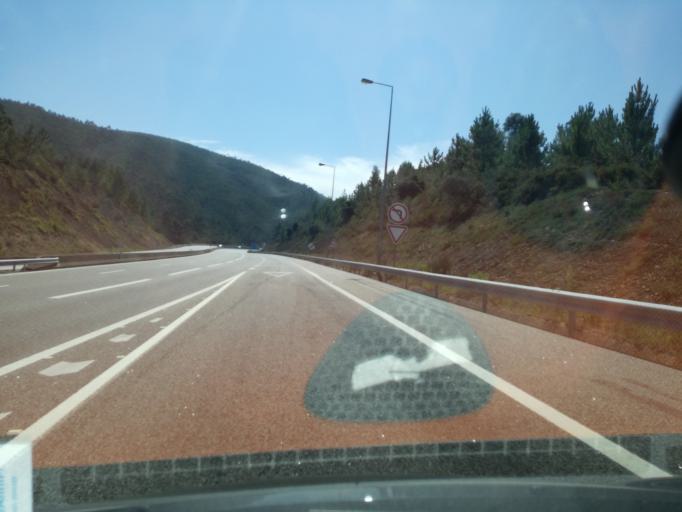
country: ES
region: Galicia
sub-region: Provincia de Pontevedra
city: O Rosal
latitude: 41.8767
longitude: -8.7875
